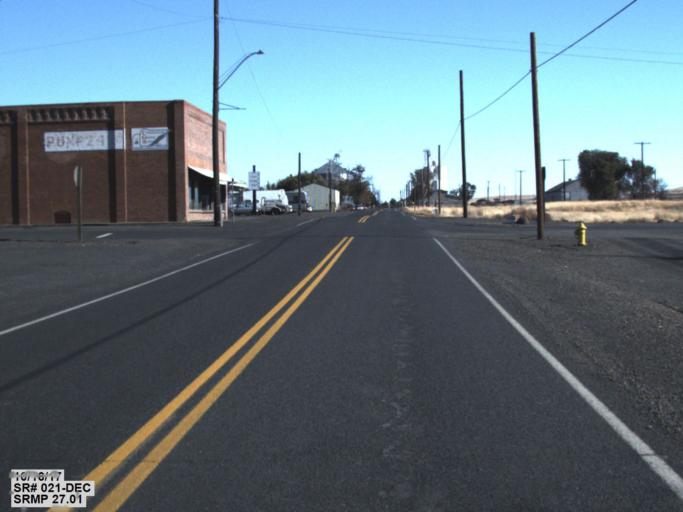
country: US
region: Washington
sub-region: Adams County
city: Ritzville
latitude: 46.9712
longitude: -118.6212
